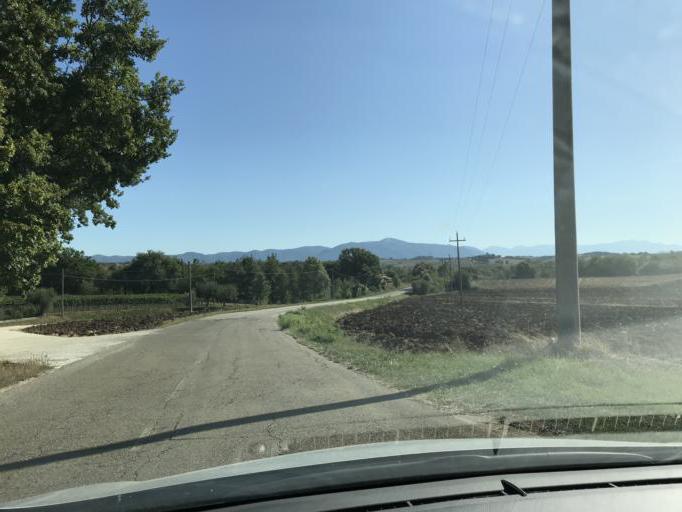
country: IT
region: Umbria
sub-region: Provincia di Terni
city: Avigliano Umbro
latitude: 42.6187
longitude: 12.4165
